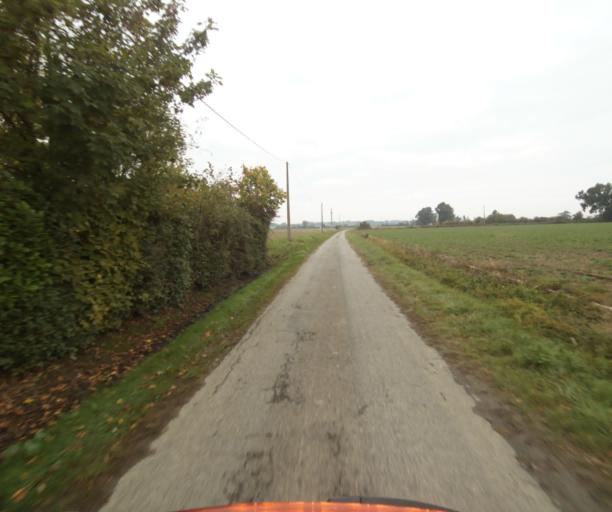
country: FR
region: Midi-Pyrenees
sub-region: Departement du Tarn-et-Garonne
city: Verdun-sur-Garonne
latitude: 43.8139
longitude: 1.2306
